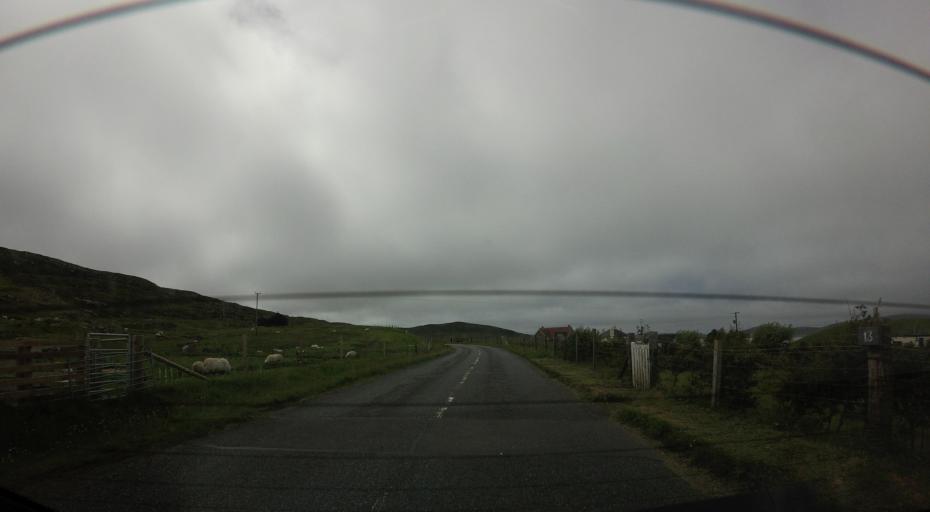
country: GB
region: Scotland
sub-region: Eilean Siar
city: Harris
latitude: 57.8688
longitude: -6.9366
